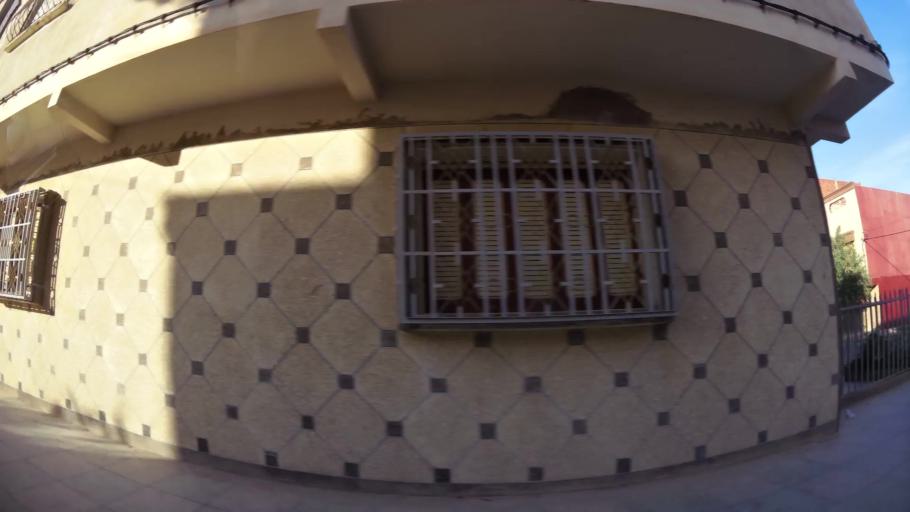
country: MA
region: Oriental
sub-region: Oujda-Angad
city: Oujda
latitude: 34.7070
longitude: -1.8989
